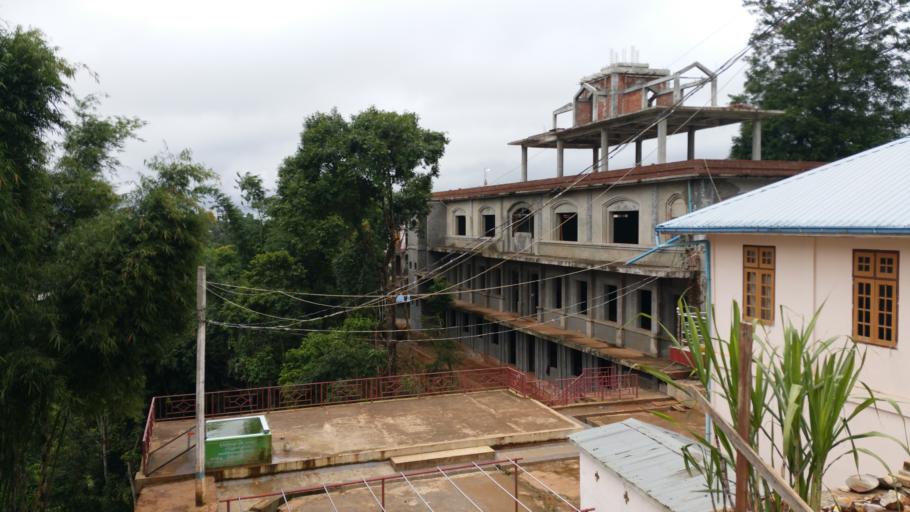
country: MM
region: Mandalay
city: Yamethin
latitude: 20.6275
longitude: 96.5567
